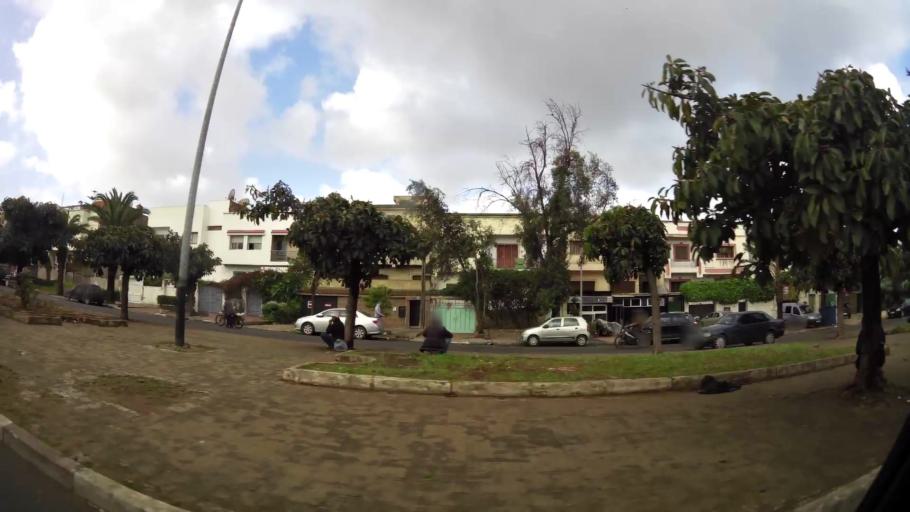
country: MA
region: Grand Casablanca
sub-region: Casablanca
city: Casablanca
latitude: 33.5598
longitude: -7.6805
